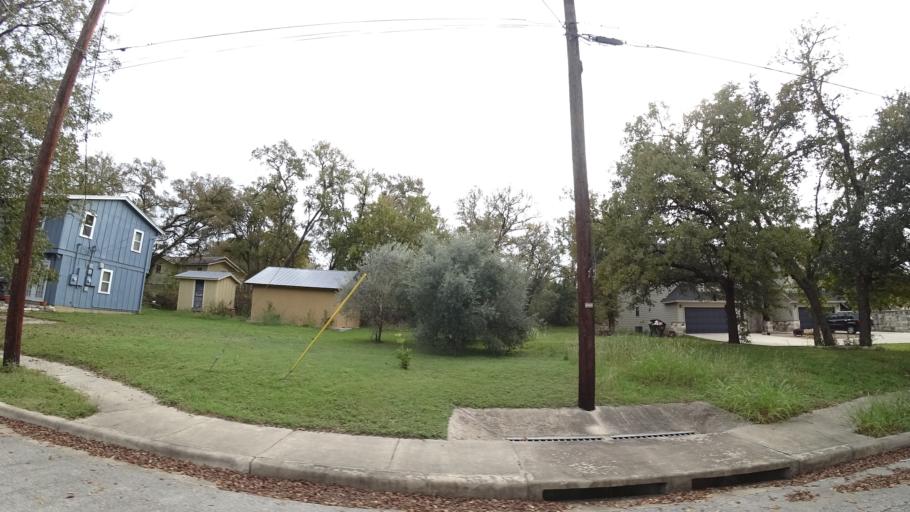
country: US
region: Texas
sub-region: Williamson County
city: Round Rock
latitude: 30.5146
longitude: -97.6735
